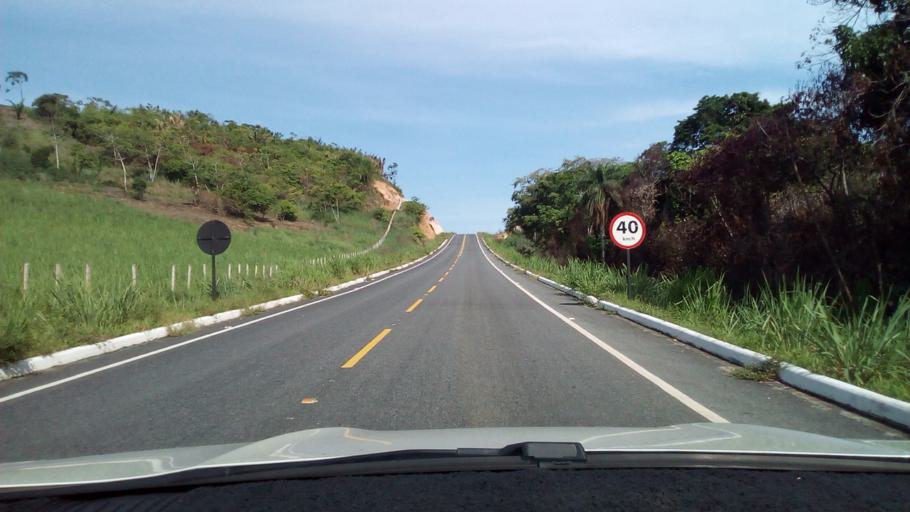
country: BR
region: Paraiba
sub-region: Bayeux
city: Bayeux
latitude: -7.0610
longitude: -34.9323
